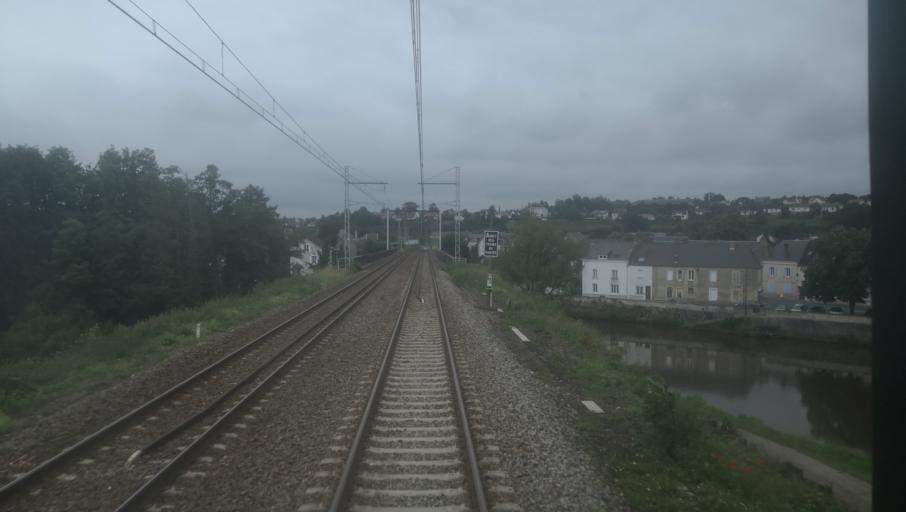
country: FR
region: Centre
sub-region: Departement de l'Indre
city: Argenton-sur-Creuse
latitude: 46.5830
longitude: 1.5251
